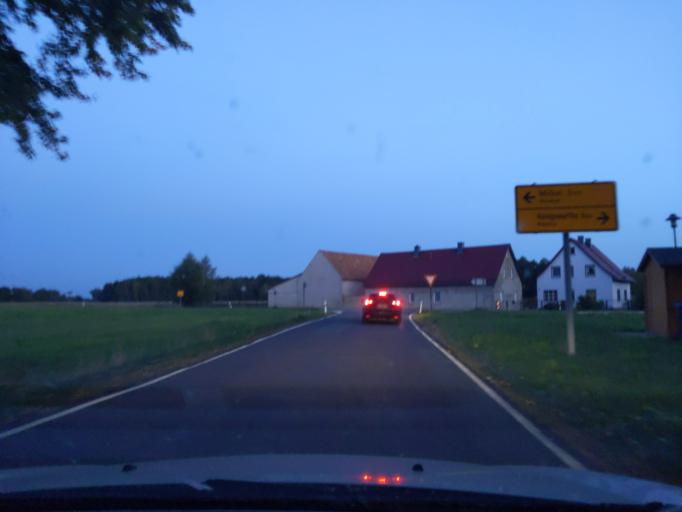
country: DE
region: Saxony
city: Radibor
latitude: 51.3048
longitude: 14.4190
